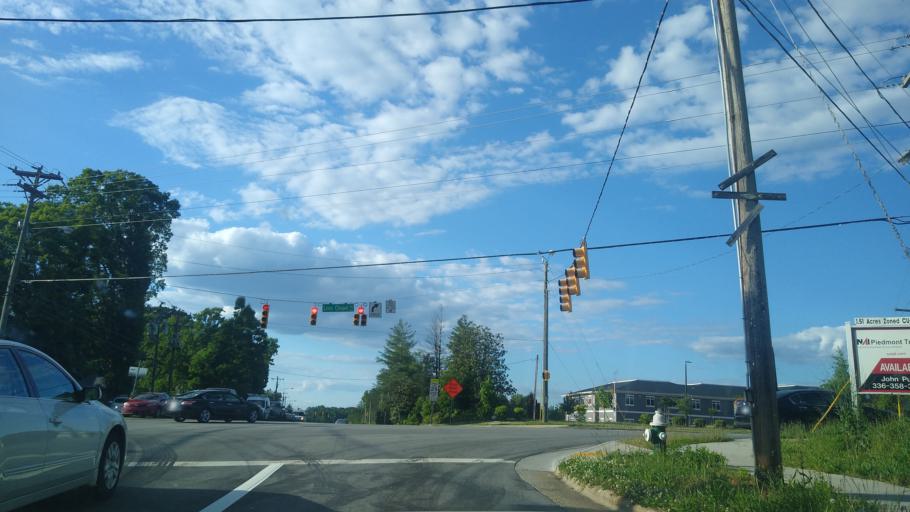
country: US
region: North Carolina
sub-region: Guilford County
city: Greensboro
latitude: 36.1401
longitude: -79.7761
